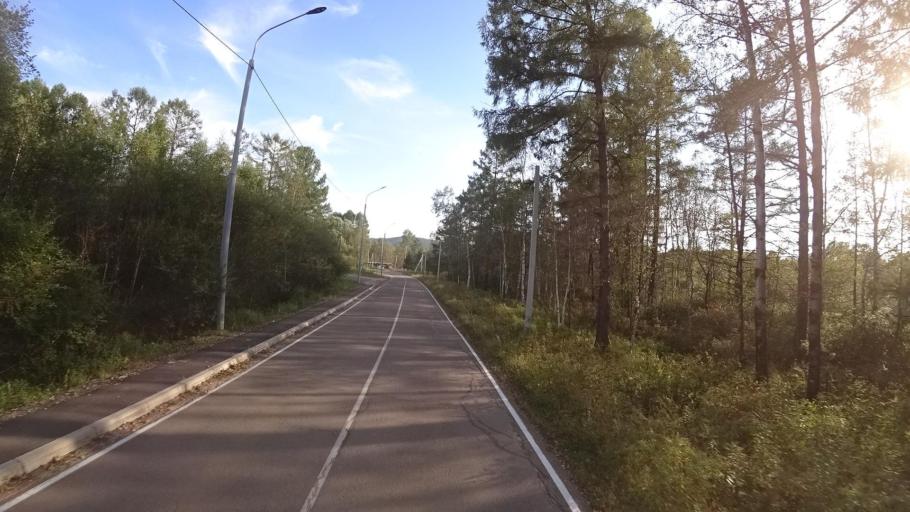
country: RU
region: Jewish Autonomous Oblast
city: Kul'dur
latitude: 49.2049
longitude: 131.6205
